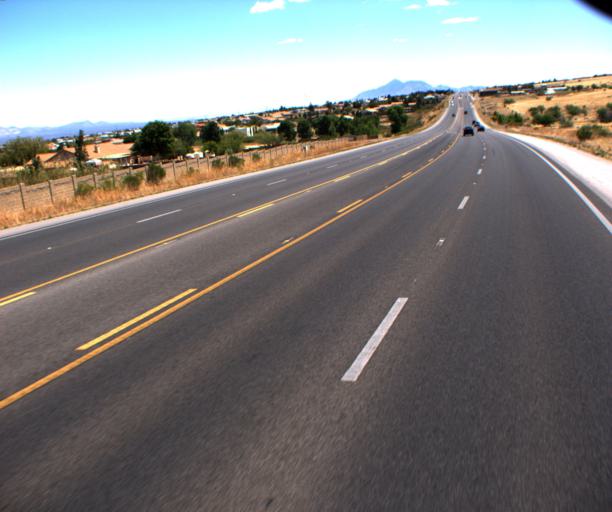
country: US
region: Arizona
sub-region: Cochise County
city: Sierra Vista Southeast
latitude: 31.4443
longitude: -110.2554
